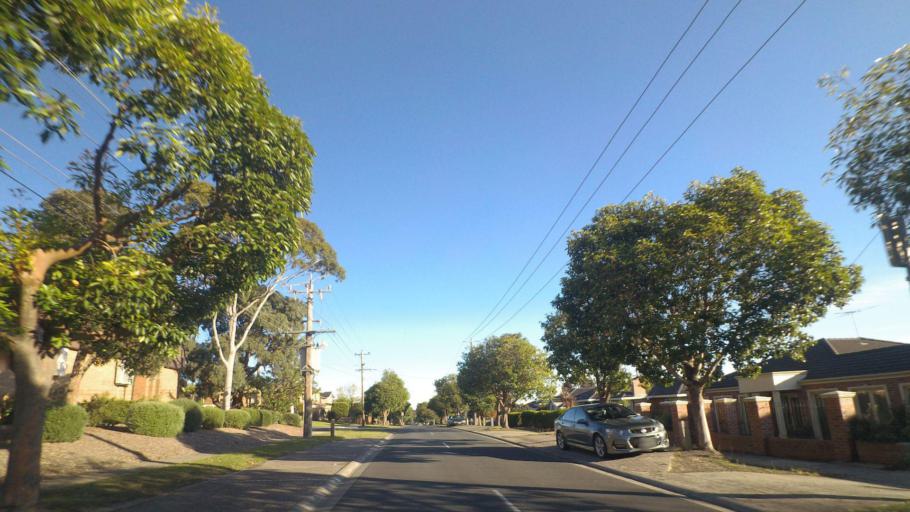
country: AU
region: Victoria
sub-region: Manningham
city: Doncaster East
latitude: -37.7910
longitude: 145.1523
